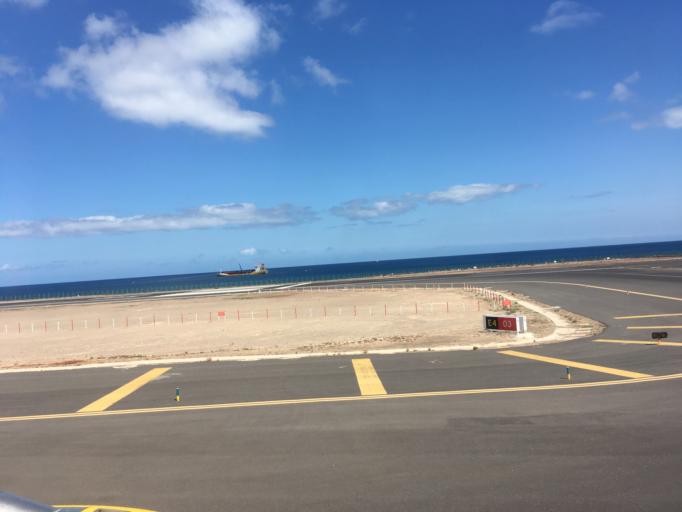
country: ES
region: Canary Islands
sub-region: Provincia de Las Palmas
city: Tias
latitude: 28.9370
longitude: -13.6122
